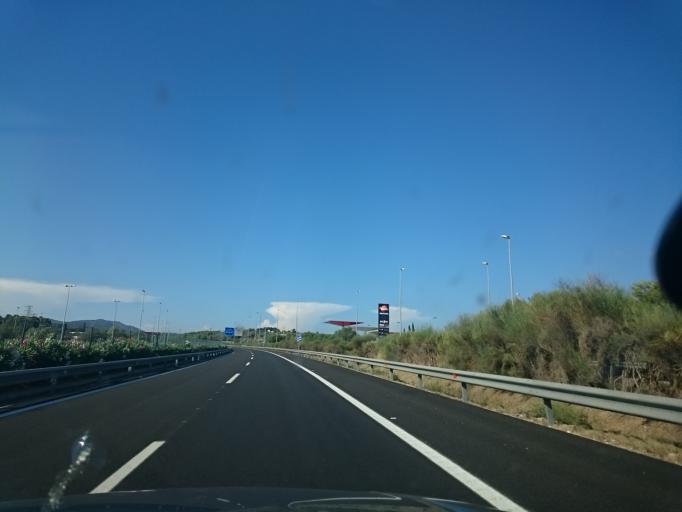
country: ES
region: Catalonia
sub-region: Provincia de Barcelona
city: Cubelles
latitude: 41.2190
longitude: 1.6744
